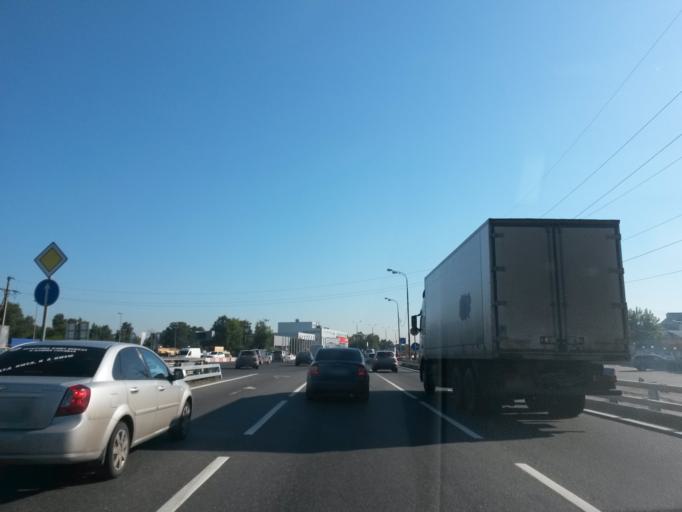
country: RU
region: Moskovskaya
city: Druzhba
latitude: 55.8847
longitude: 37.7311
